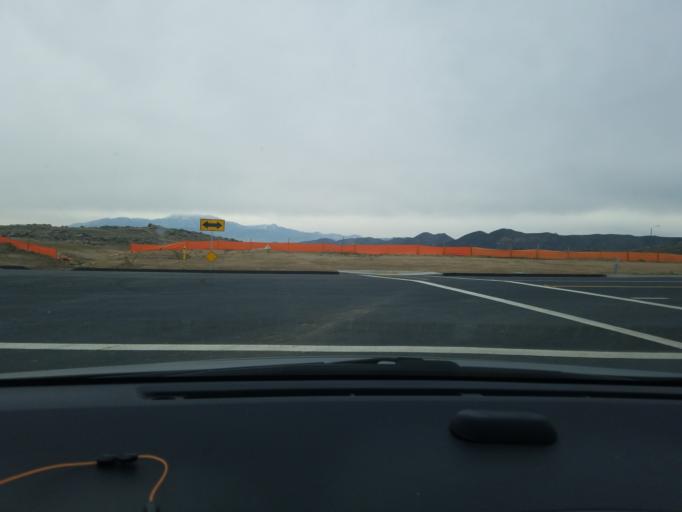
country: US
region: California
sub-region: Riverside County
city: Winchester
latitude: 33.6957
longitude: -117.0938
